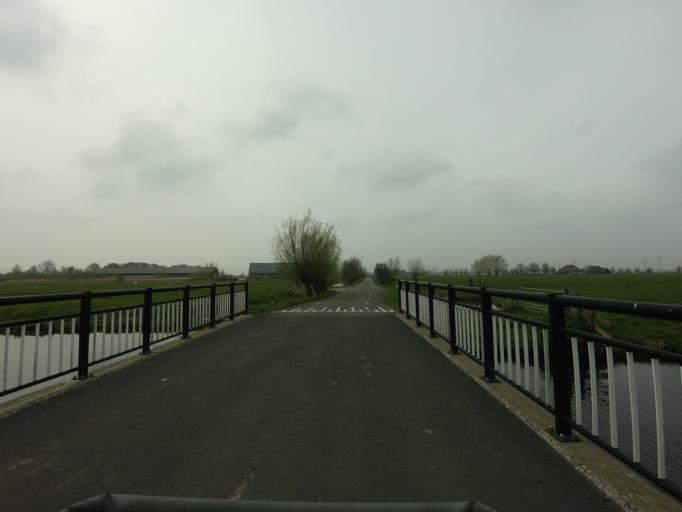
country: NL
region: South Holland
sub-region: Molenwaard
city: Nieuw-Lekkerland
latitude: 51.9196
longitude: 4.6609
